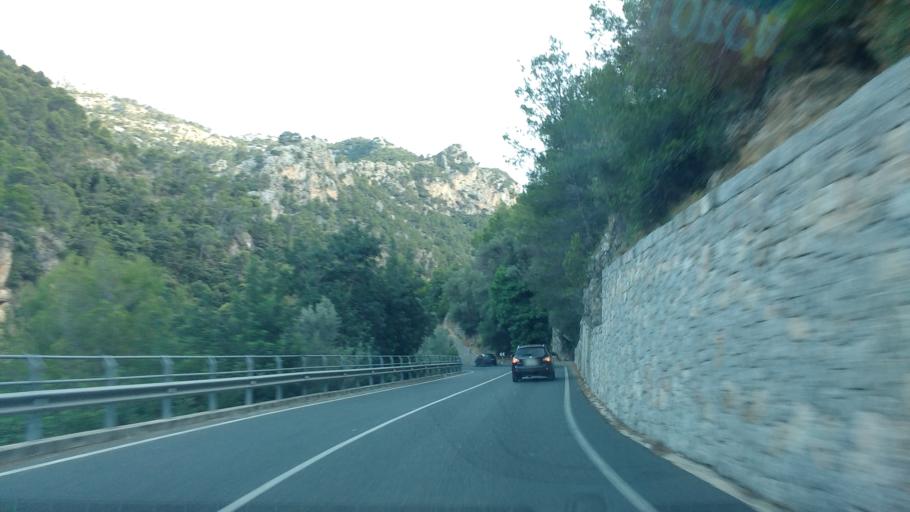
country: ES
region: Balearic Islands
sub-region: Illes Balears
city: Soller
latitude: 39.7544
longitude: 2.7069
